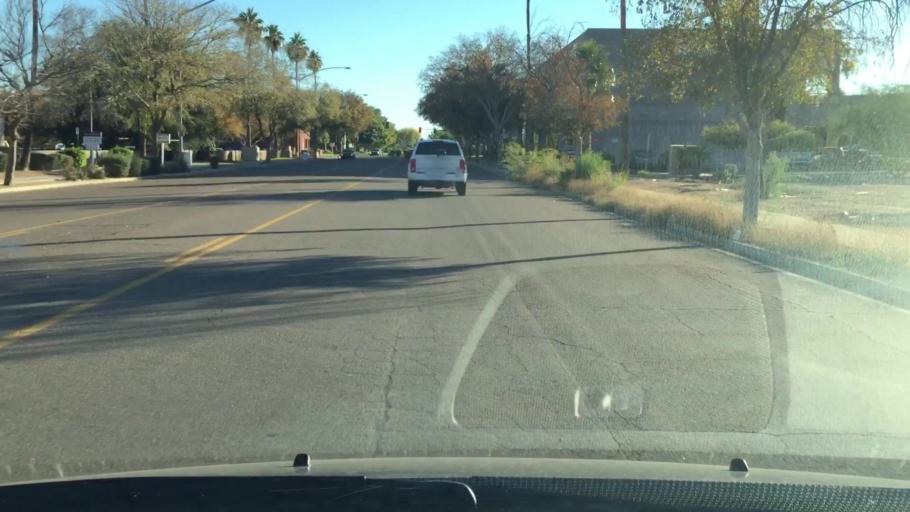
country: US
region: Arizona
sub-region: Maricopa County
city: Gilbert
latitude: 33.3811
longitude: -111.7441
